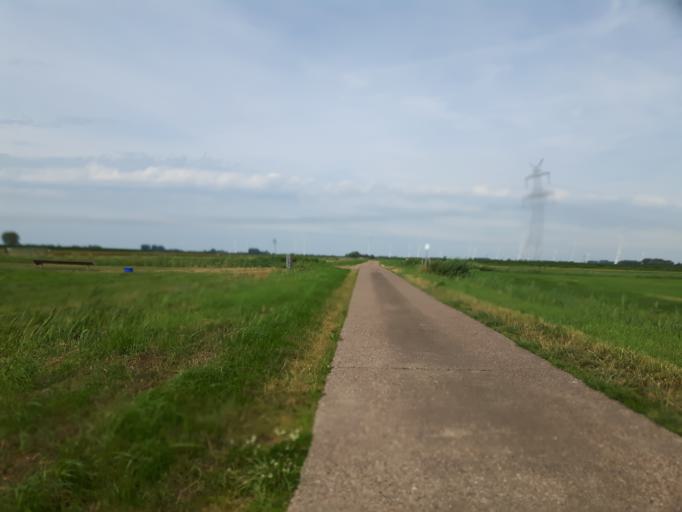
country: DE
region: Lower Saxony
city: Elsfleth
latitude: 53.2609
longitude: 8.4232
